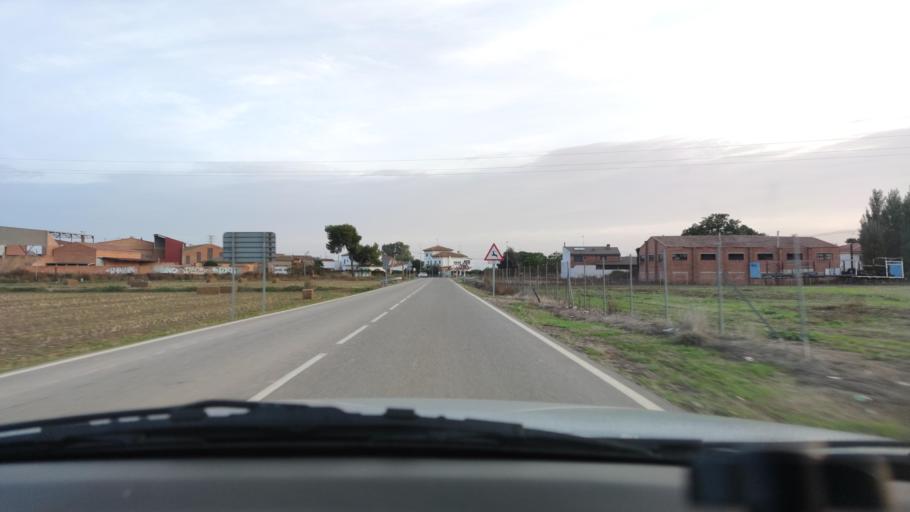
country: ES
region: Catalonia
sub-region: Provincia de Lleida
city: Mollerussa
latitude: 41.6302
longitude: 0.8759
